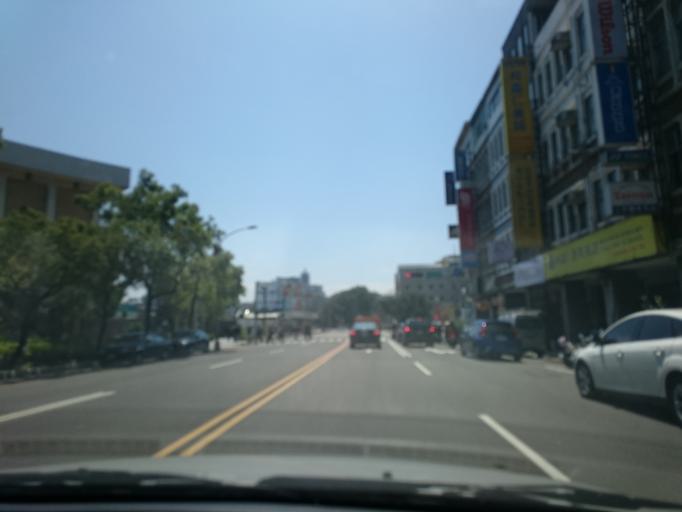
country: TW
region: Taiwan
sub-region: Taichung City
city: Taichung
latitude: 24.1478
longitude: 120.6867
